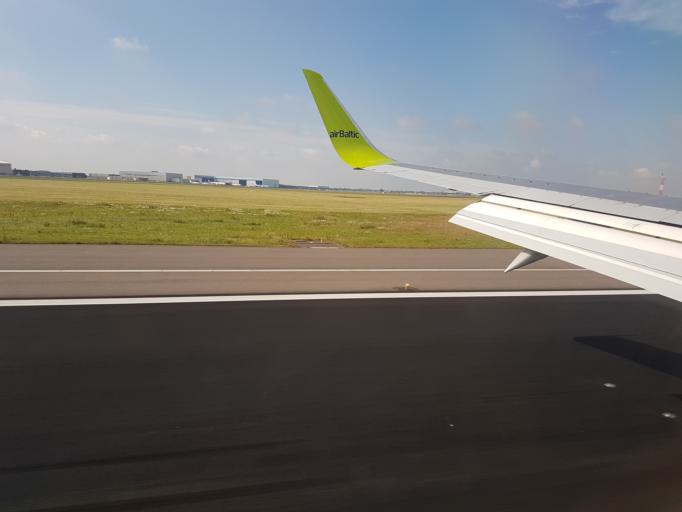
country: NL
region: North Holland
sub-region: Gemeente Aalsmeer
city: Aalsmeer
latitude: 52.3182
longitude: 4.7915
